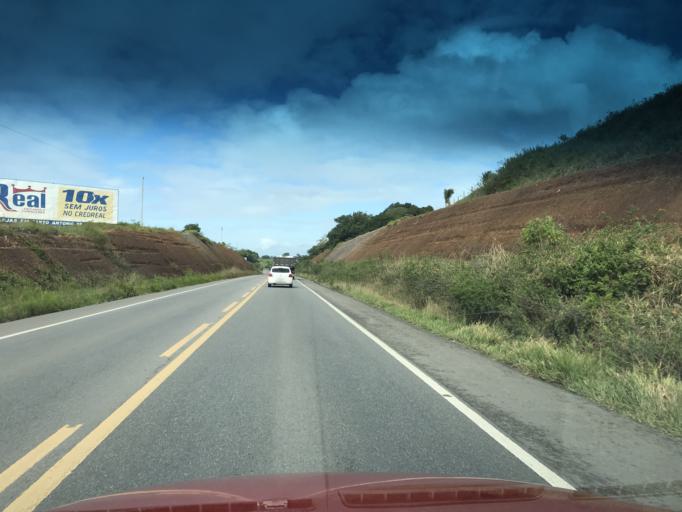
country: BR
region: Bahia
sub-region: Conceicao Do Almeida
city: Muritiba
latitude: -12.9002
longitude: -39.2362
